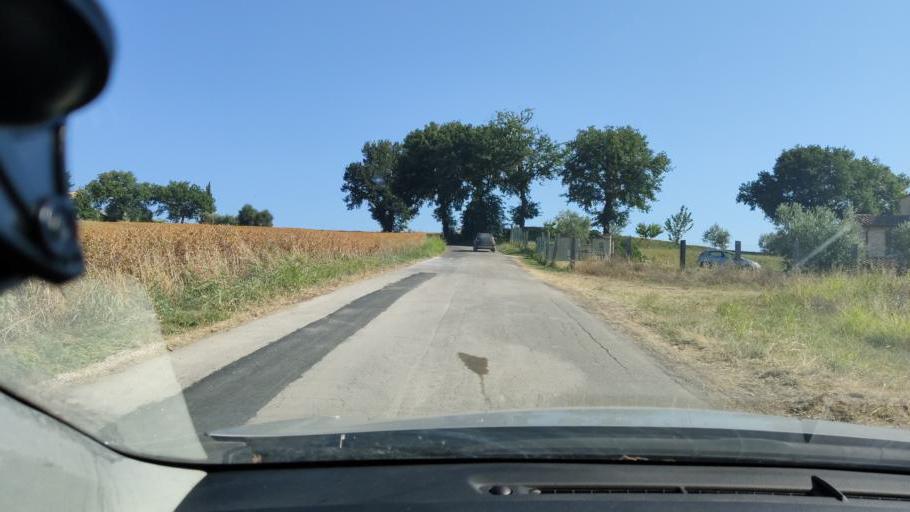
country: IT
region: Umbria
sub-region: Provincia di Terni
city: Amelia
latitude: 42.5372
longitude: 12.4311
